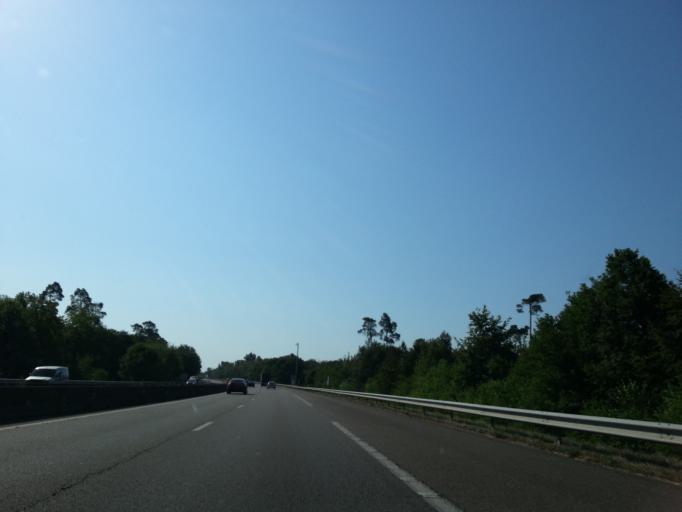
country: FR
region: Alsace
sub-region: Departement du Bas-Rhin
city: Brumath
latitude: 48.7112
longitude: 7.7012
